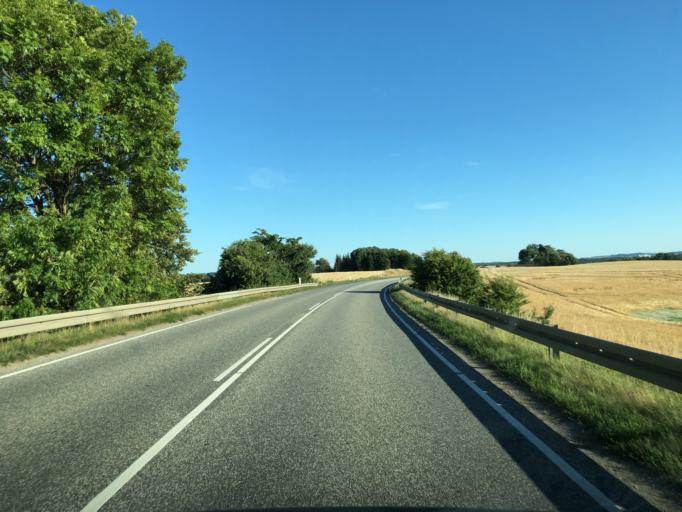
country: DK
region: Central Jutland
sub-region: Skanderborg Kommune
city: Stilling
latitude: 56.0766
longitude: 9.9758
